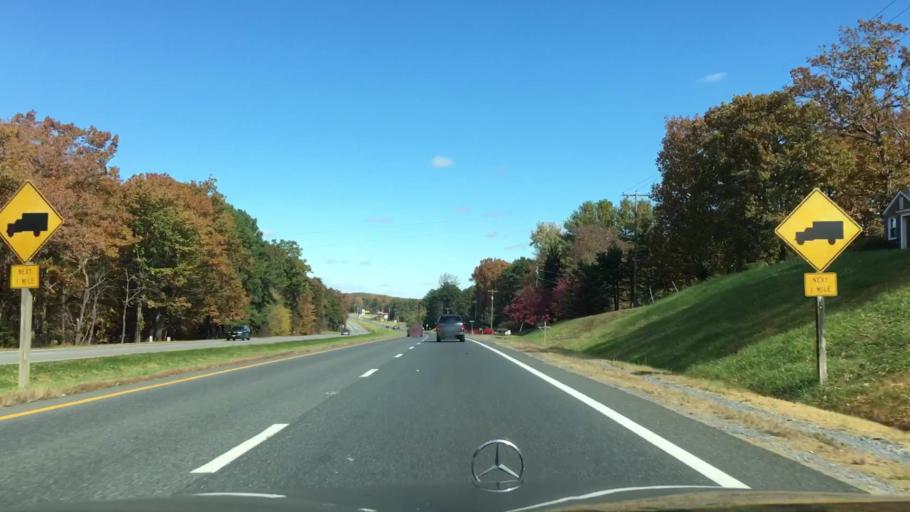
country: US
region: Virginia
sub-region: Campbell County
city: Rustburg
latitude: 37.2216
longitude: -79.1916
